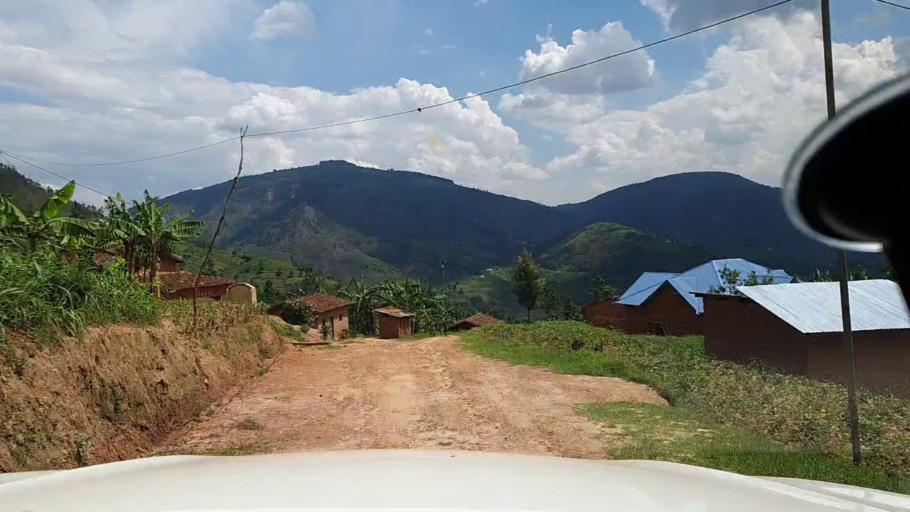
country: RW
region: Southern Province
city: Gitarama
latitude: -1.8423
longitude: 29.8153
